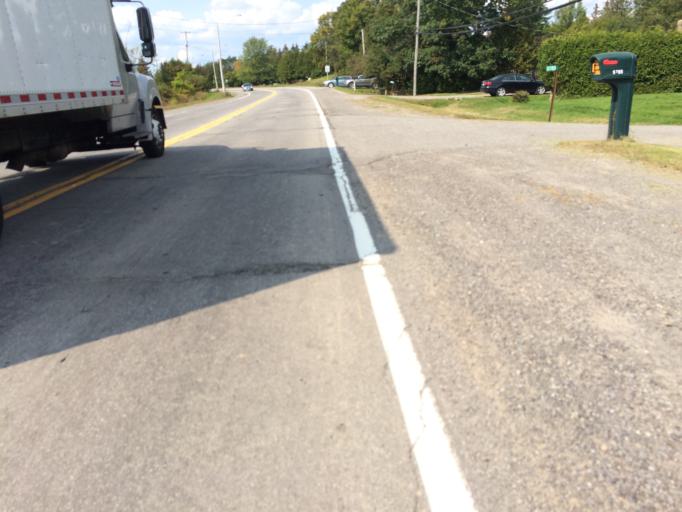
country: CA
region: Ontario
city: Bells Corners
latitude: 45.2139
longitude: -75.6652
